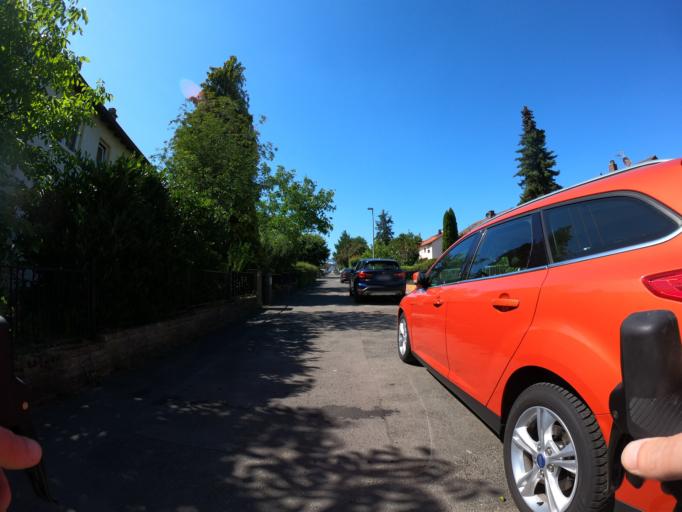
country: DE
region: Hesse
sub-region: Regierungsbezirk Darmstadt
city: Eschborn
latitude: 50.1402
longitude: 8.5589
